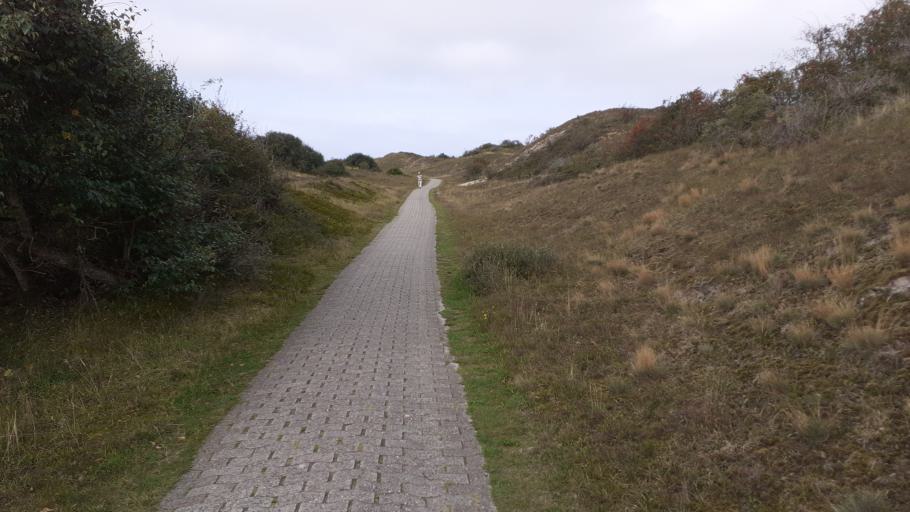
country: DE
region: Lower Saxony
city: Spiekeroog
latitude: 53.7763
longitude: 7.7099
